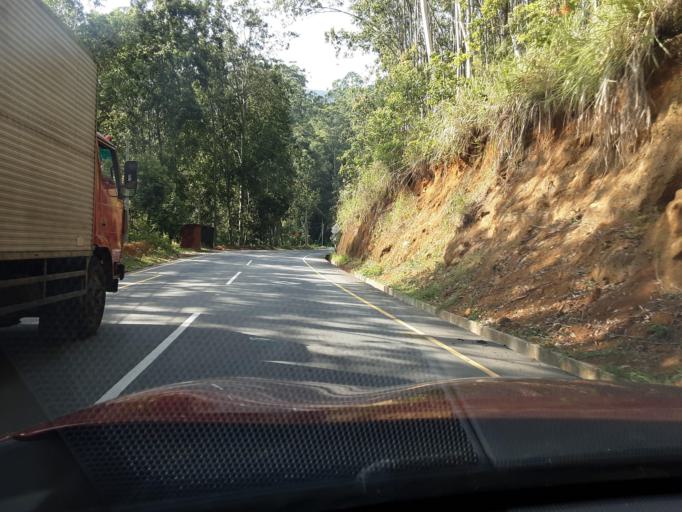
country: LK
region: Uva
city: Badulla
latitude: 6.9638
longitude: 81.0954
